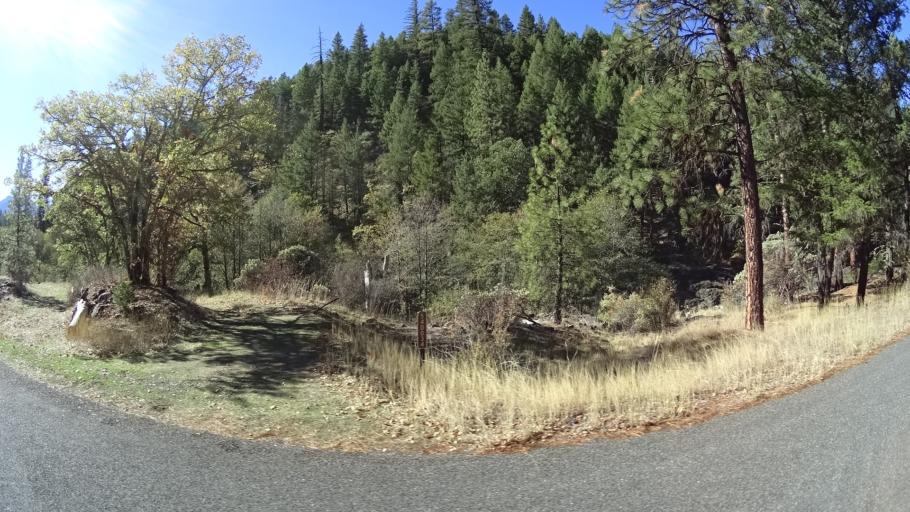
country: US
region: California
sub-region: Trinity County
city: Weaverville
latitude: 41.1401
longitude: -123.0976
